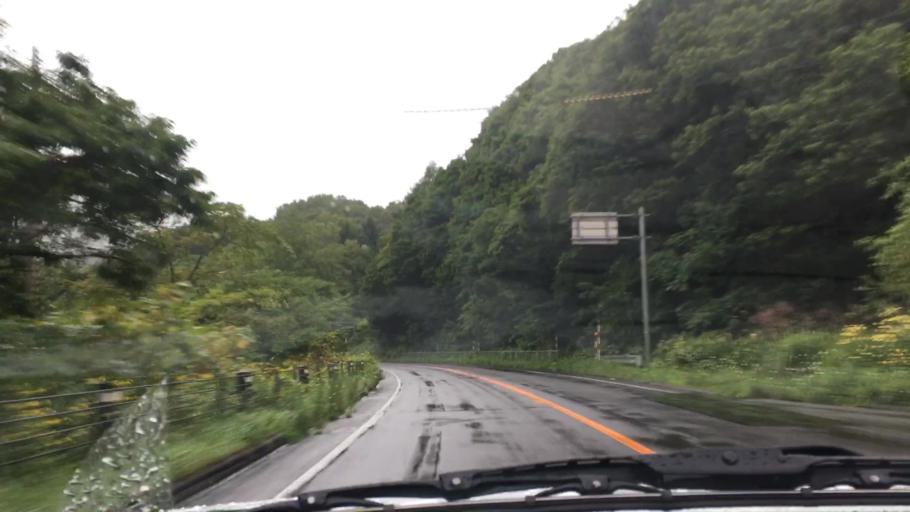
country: JP
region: Hokkaido
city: Niseko Town
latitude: 42.6030
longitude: 140.6176
